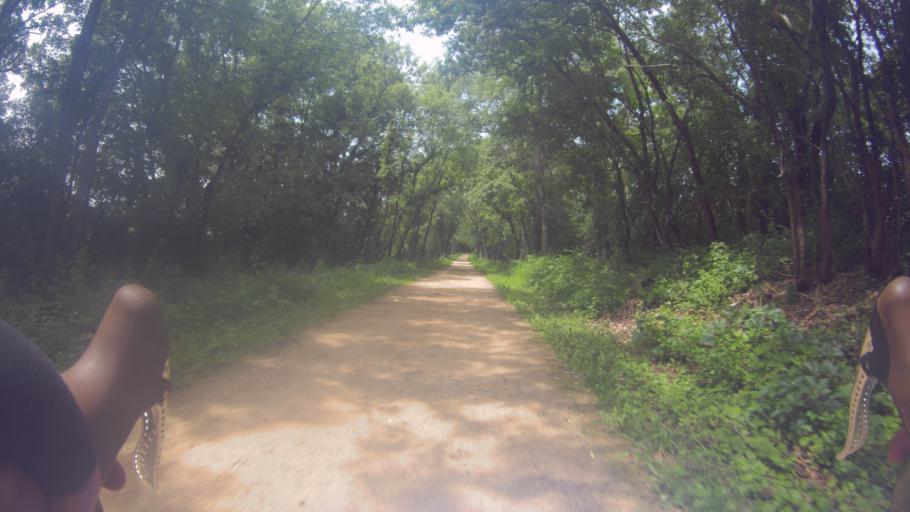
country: US
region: Wisconsin
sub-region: Dane County
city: Mount Horeb
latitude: 43.0154
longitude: -89.7136
